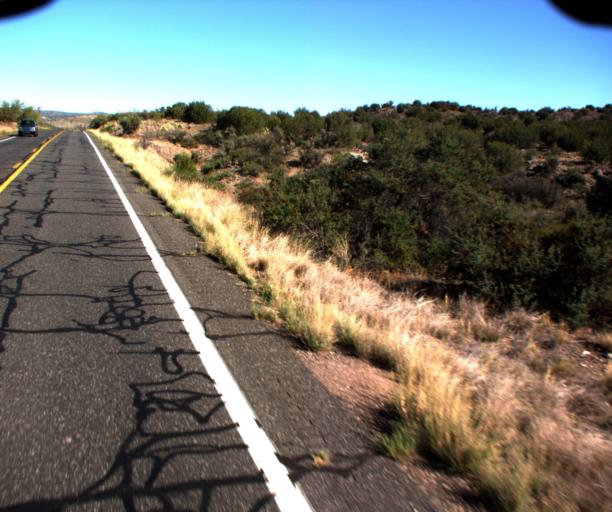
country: US
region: Arizona
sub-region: Yavapai County
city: Big Park
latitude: 34.7084
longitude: -111.7740
